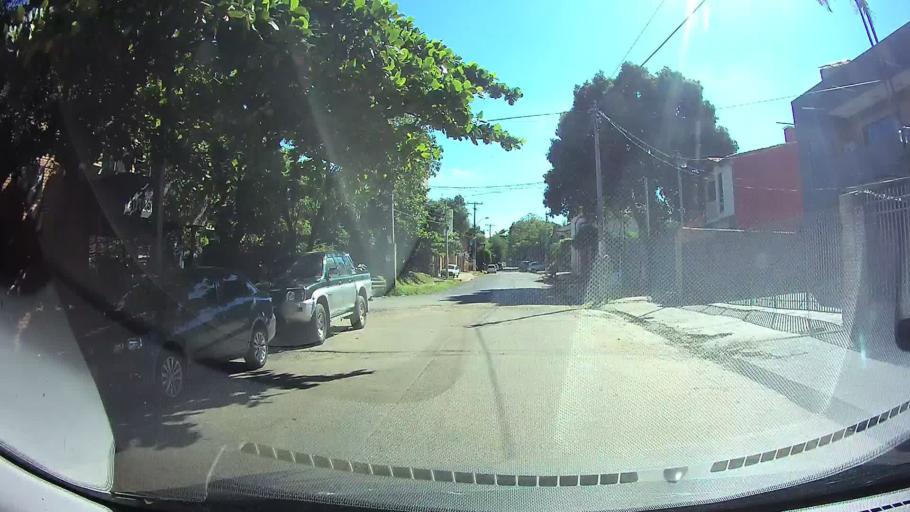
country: PY
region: Central
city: Fernando de la Mora
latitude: -25.3120
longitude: -57.5591
